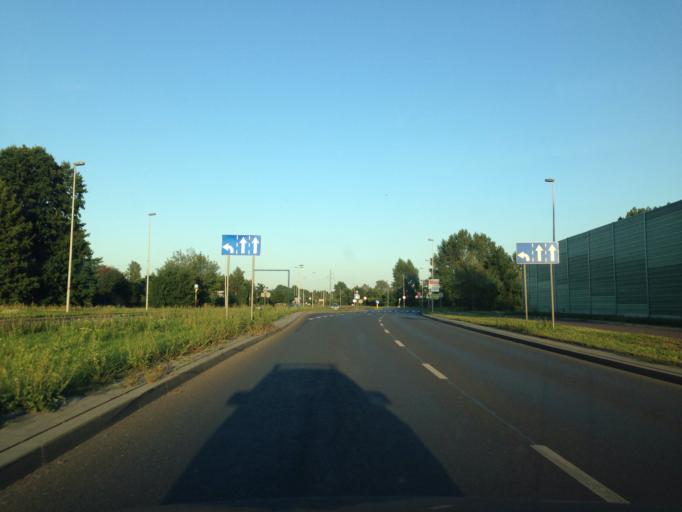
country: PL
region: Kujawsko-Pomorskie
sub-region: Powiat torunski
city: Lubicz Dolny
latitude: 53.0366
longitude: 18.6839
